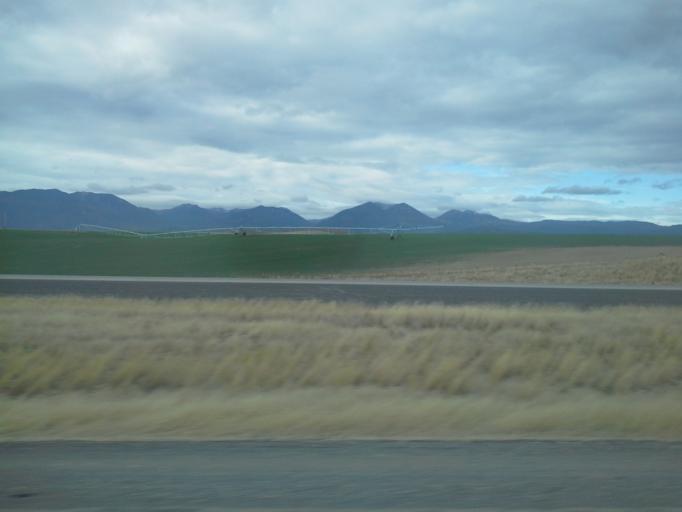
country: US
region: Oregon
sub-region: Union County
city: Union
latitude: 44.9952
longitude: -117.9012
